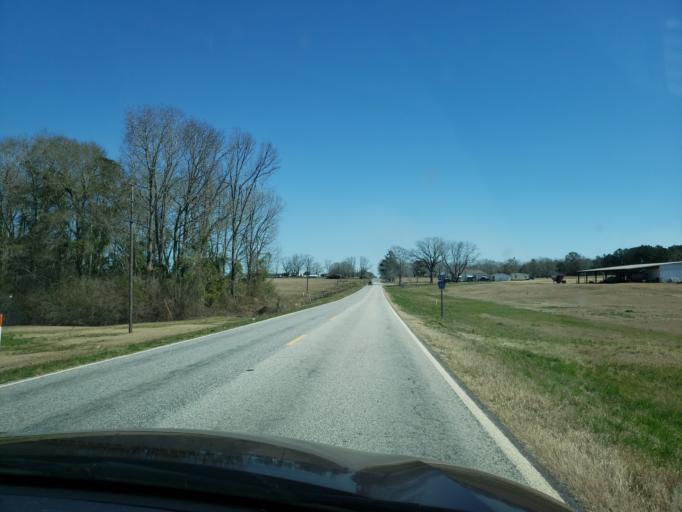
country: US
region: Alabama
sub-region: Elmore County
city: Tallassee
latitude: 32.5813
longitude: -85.7761
